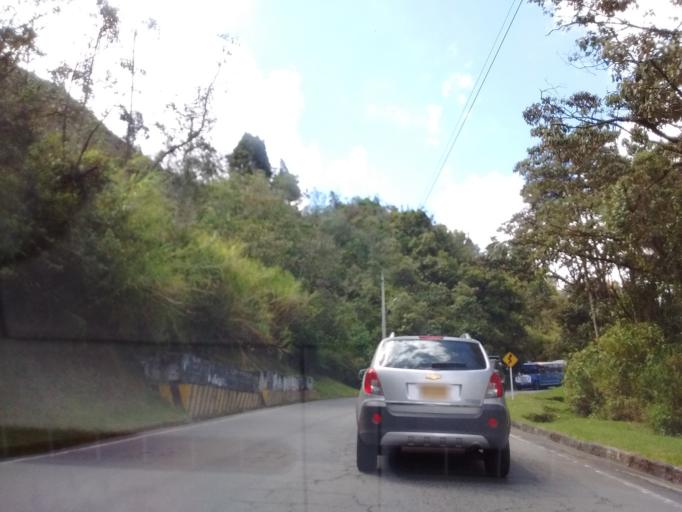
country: CO
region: Antioquia
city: Medellin
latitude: 6.2280
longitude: -75.5036
